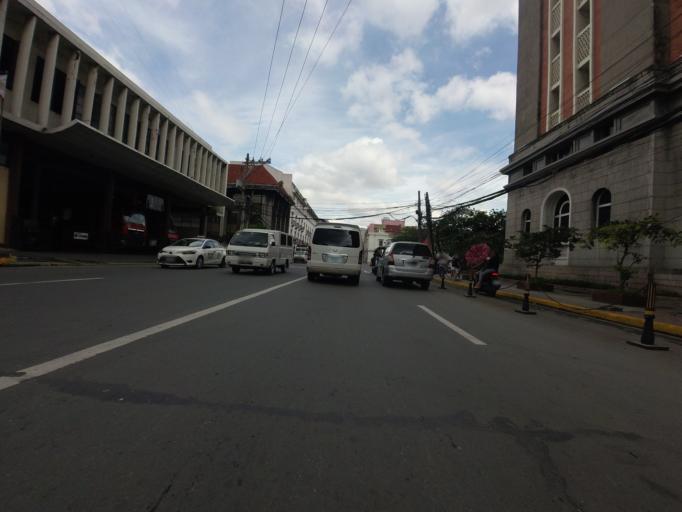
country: PH
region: Metro Manila
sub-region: City of Manila
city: Port Area
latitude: 14.5920
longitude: 120.9723
